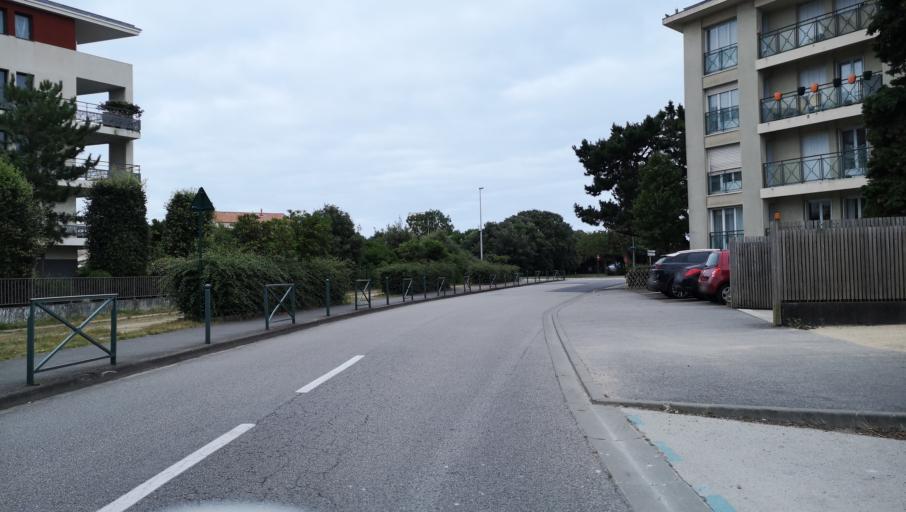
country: FR
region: Pays de la Loire
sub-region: Departement de la Vendee
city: Les Sables-d'Olonne
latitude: 46.5014
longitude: -1.7850
